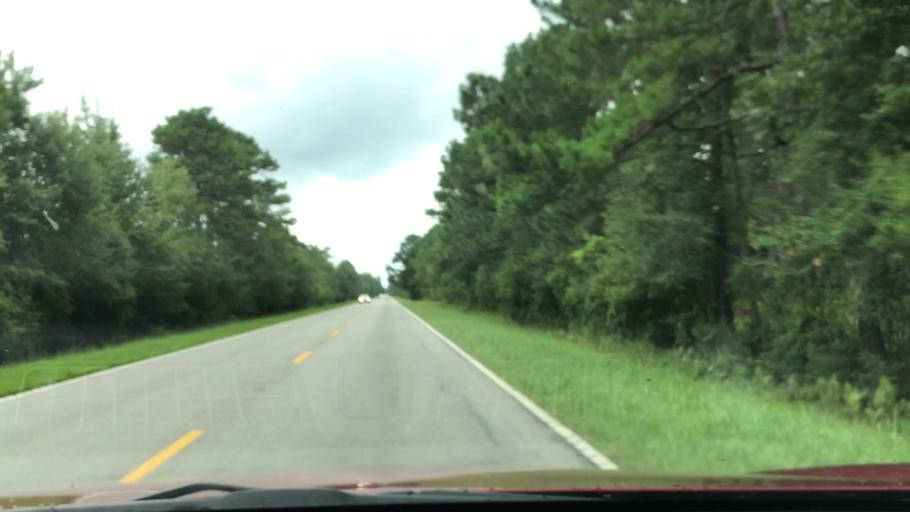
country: US
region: South Carolina
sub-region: Georgetown County
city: Georgetown
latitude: 33.5411
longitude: -79.2291
